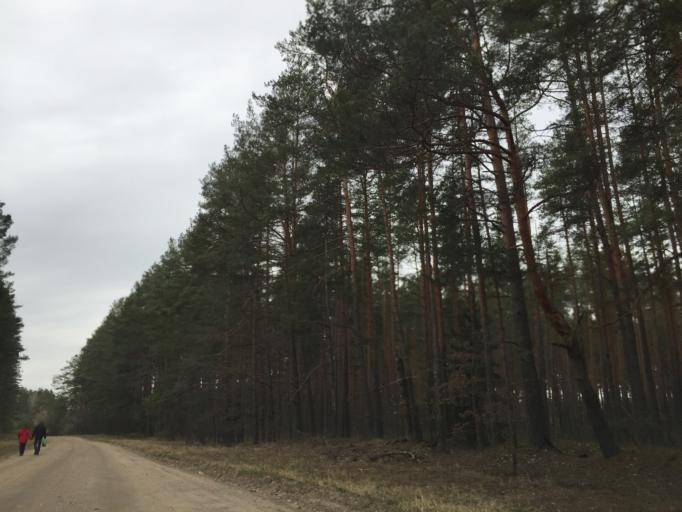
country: LV
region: Ilukste
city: Ilukste
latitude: 55.9787
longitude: 26.3265
